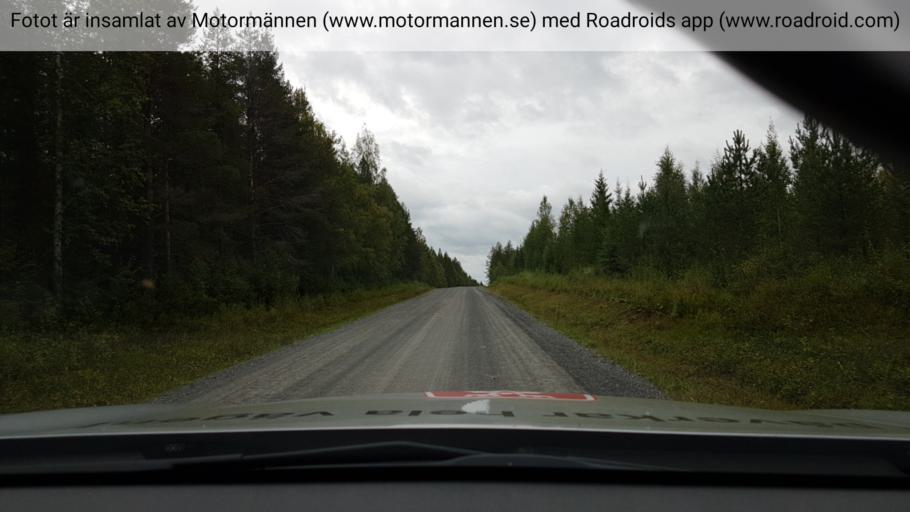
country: SE
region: Vaesterbotten
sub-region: Skelleftea Kommun
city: Forsbacka
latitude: 64.7787
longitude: 20.5152
